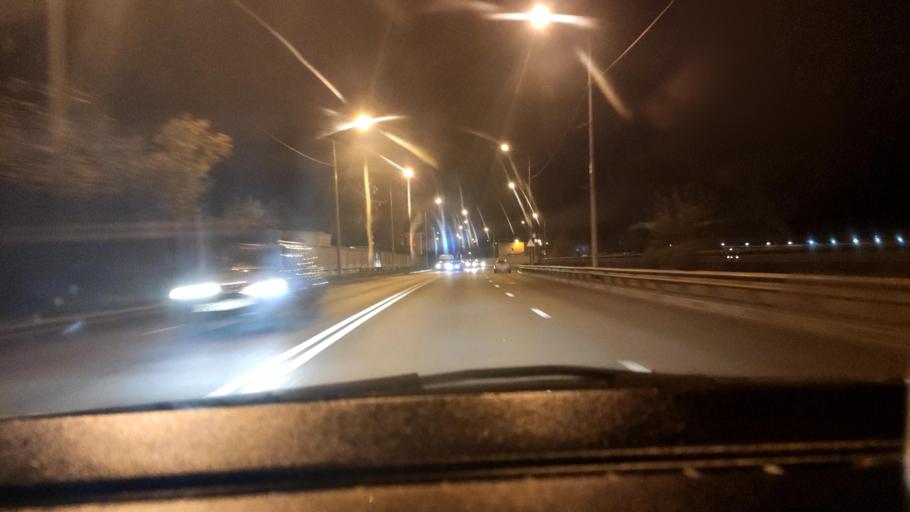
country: RU
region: Voronezj
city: Voronezh
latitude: 51.6827
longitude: 39.2282
